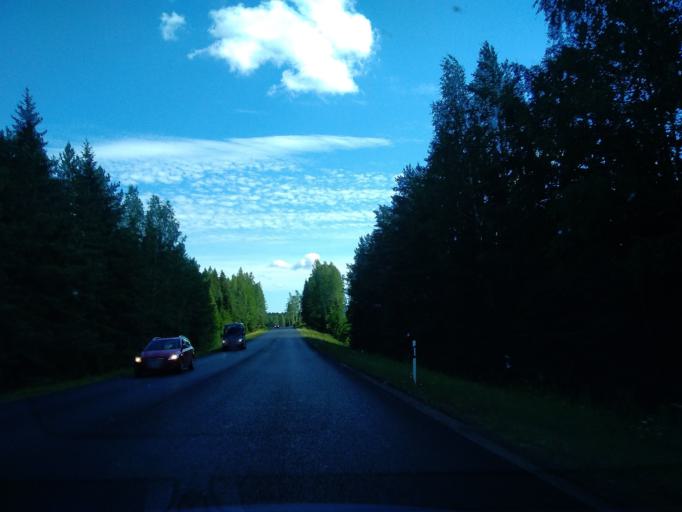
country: FI
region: Haeme
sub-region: Haemeenlinna
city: Renko
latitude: 60.9384
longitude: 24.3785
